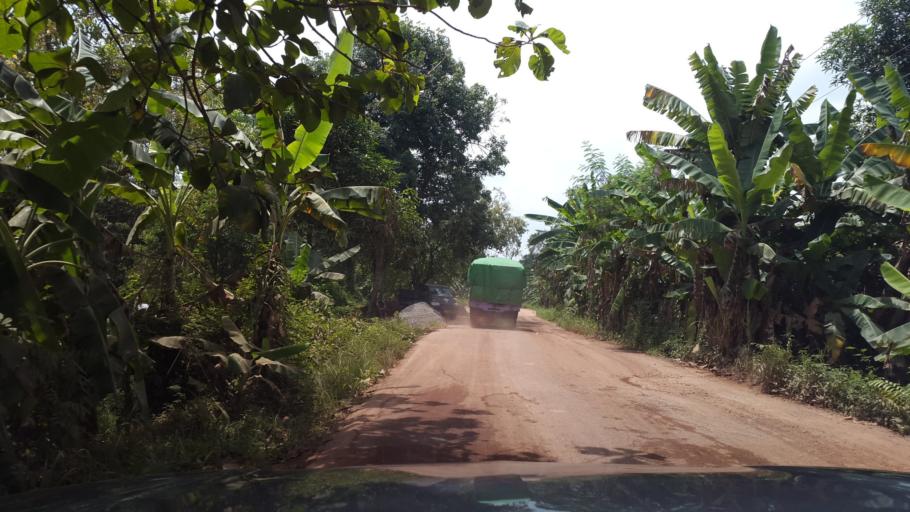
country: ID
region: South Sumatra
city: Tanjungraja
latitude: -3.1796
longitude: 104.8567
